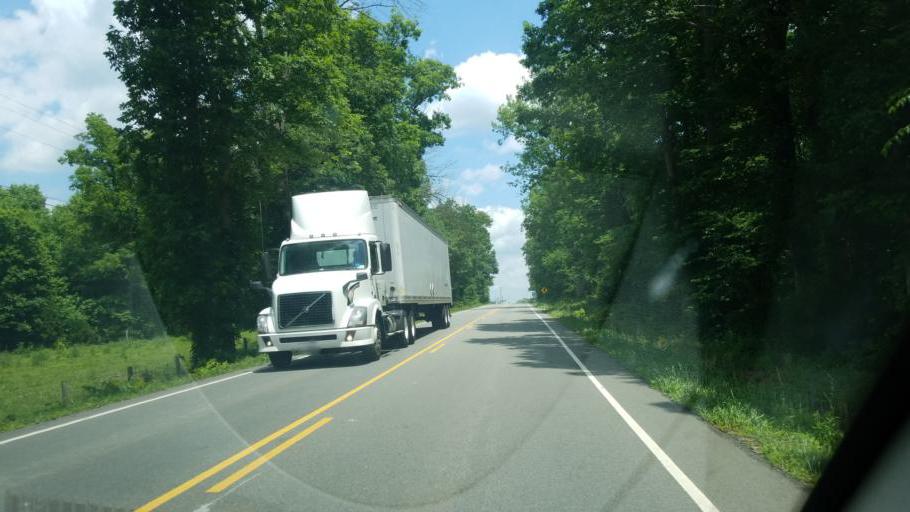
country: US
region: Virginia
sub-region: Buckingham County
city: Buckingham
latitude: 37.5540
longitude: -78.5886
